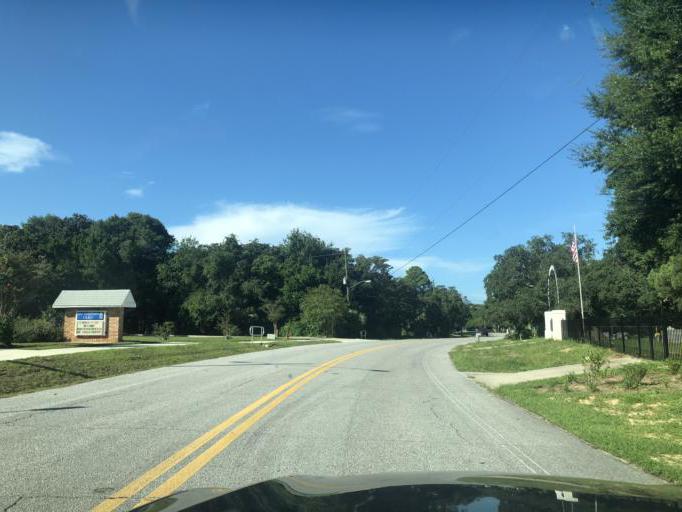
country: US
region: Florida
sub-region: Okaloosa County
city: Destin
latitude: 30.4008
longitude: -86.5095
